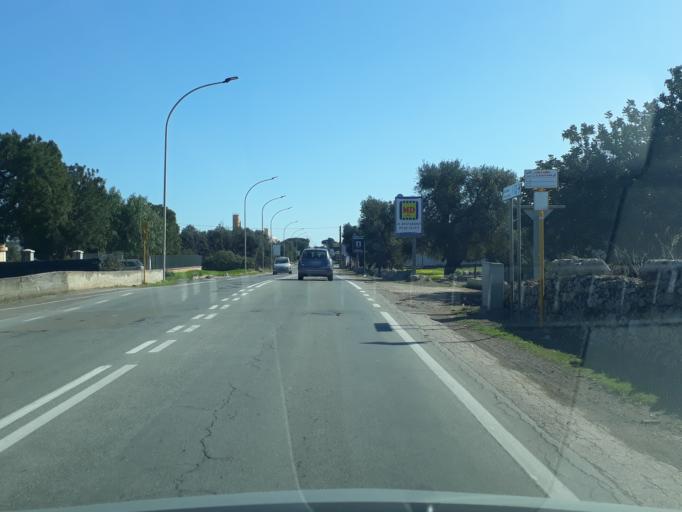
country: IT
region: Apulia
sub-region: Provincia di Bari
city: Monopoli
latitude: 40.9668
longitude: 17.2719
